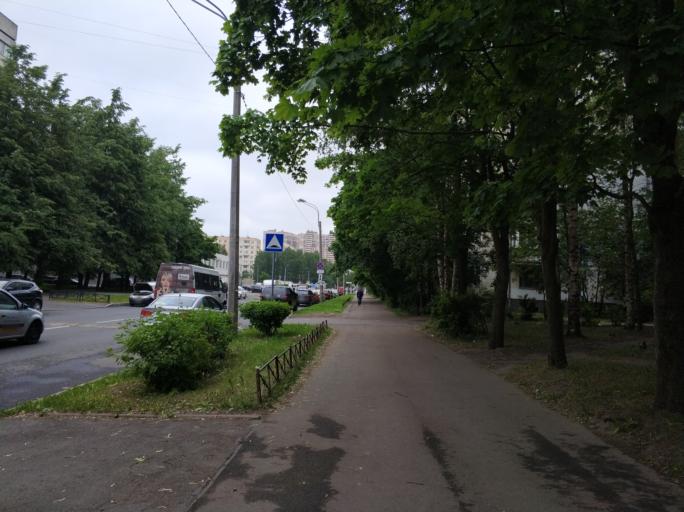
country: RU
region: St.-Petersburg
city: Grazhdanka
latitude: 60.0348
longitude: 30.3901
